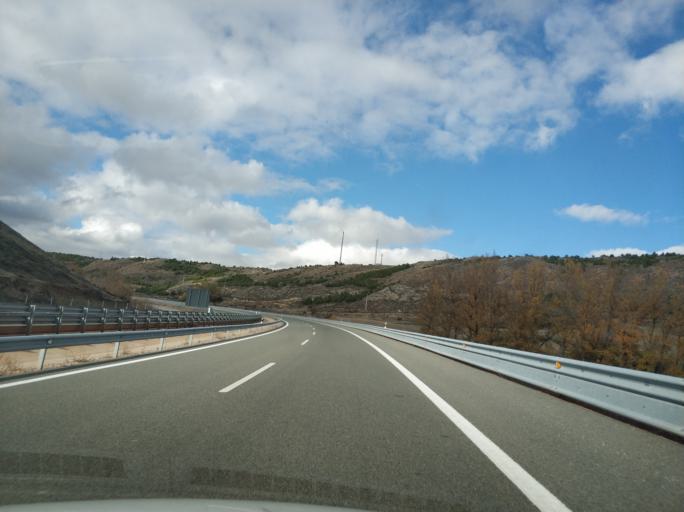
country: ES
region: Castille and Leon
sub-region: Provincia de Soria
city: Medinaceli
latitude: 41.1898
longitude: -2.4316
